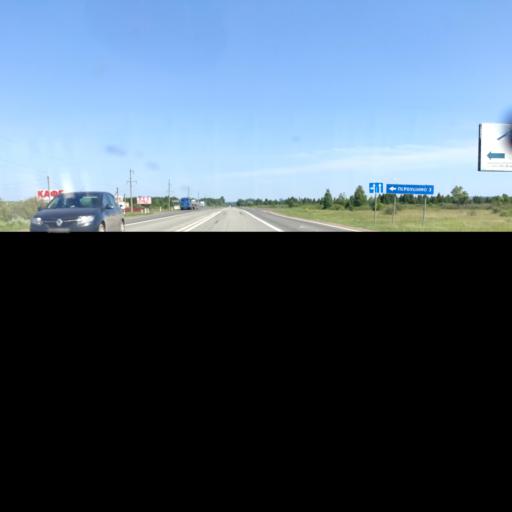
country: RU
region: Bashkortostan
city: Blagoveshchensk
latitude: 54.9882
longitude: 55.7741
